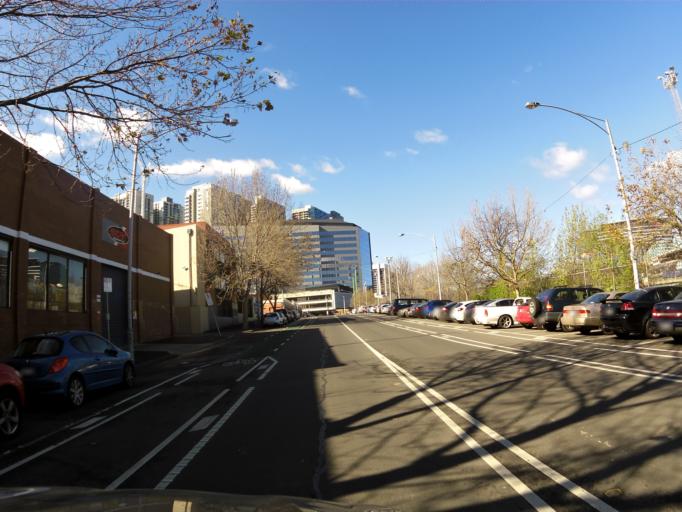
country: AU
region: Victoria
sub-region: Melbourne
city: West Melbourne
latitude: -37.8120
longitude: 144.9483
